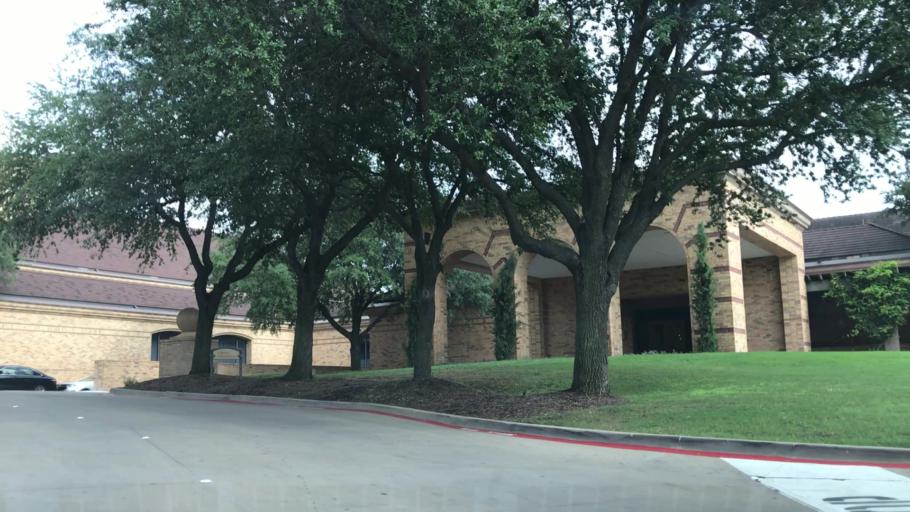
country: US
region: Texas
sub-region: Dallas County
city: Irving
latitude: 32.8628
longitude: -96.9592
